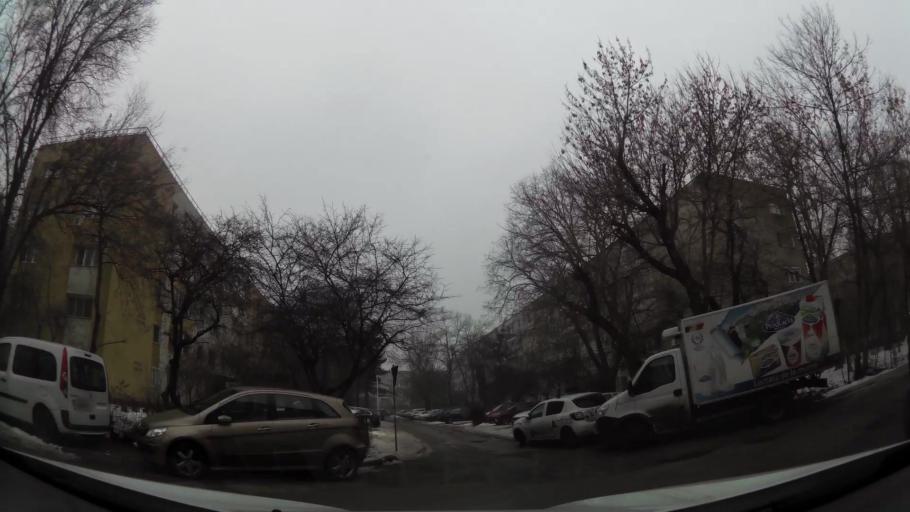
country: RO
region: Ilfov
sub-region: Comuna Chiajna
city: Rosu
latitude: 44.4417
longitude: 26.0152
